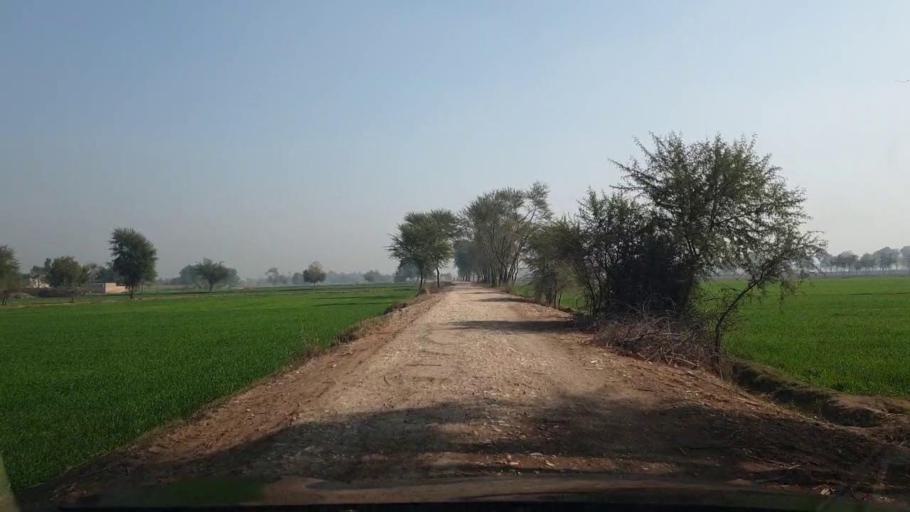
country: PK
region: Sindh
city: Ubauro
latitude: 28.1127
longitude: 69.7448
